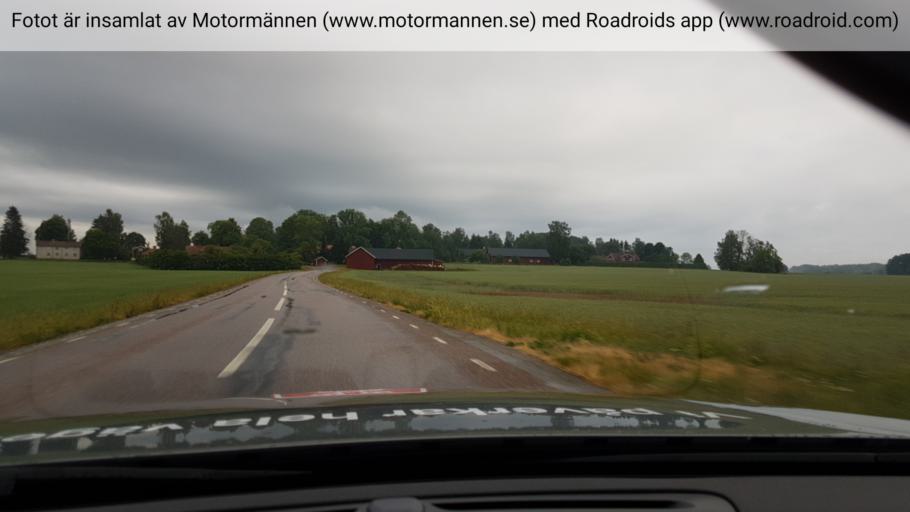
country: SE
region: Vaestmanland
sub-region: Surahammars Kommun
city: Ramnas
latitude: 59.9152
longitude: 16.3203
